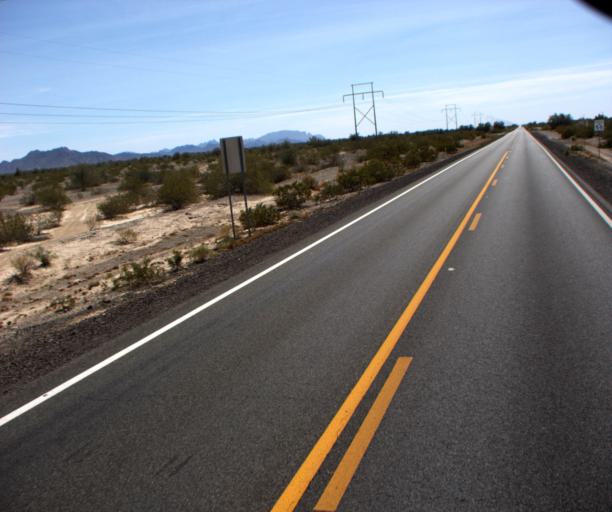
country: US
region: Arizona
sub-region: La Paz County
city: Quartzsite
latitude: 33.6490
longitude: -114.2171
